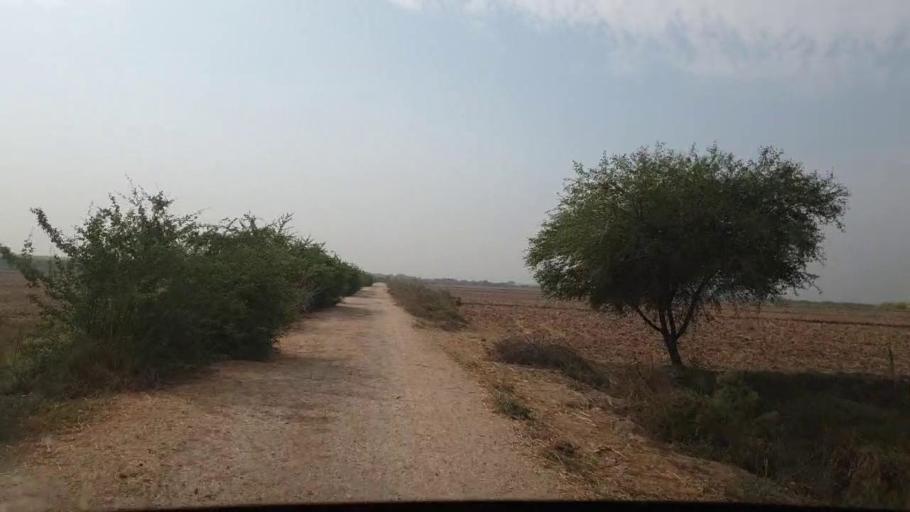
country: PK
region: Sindh
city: Chuhar Jamali
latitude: 24.4116
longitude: 67.9385
